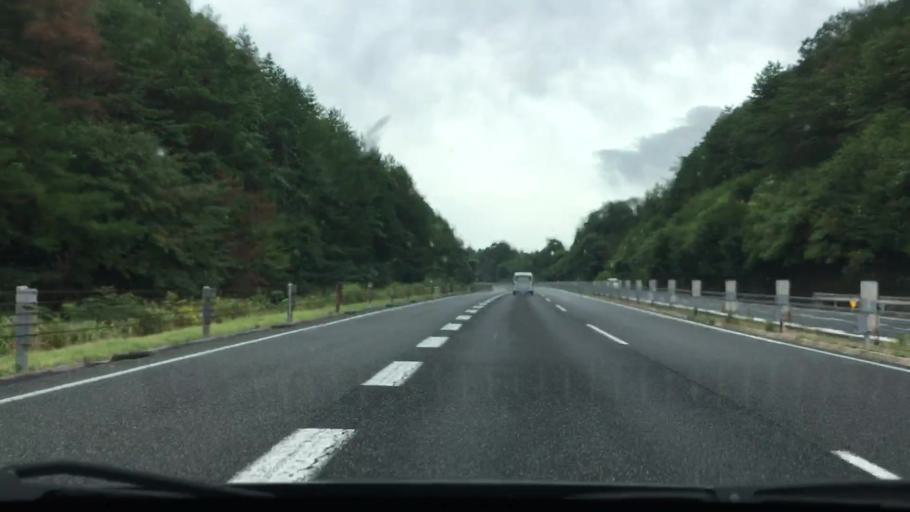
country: JP
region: Hiroshima
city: Hiroshima-shi
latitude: 34.6312
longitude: 132.5128
